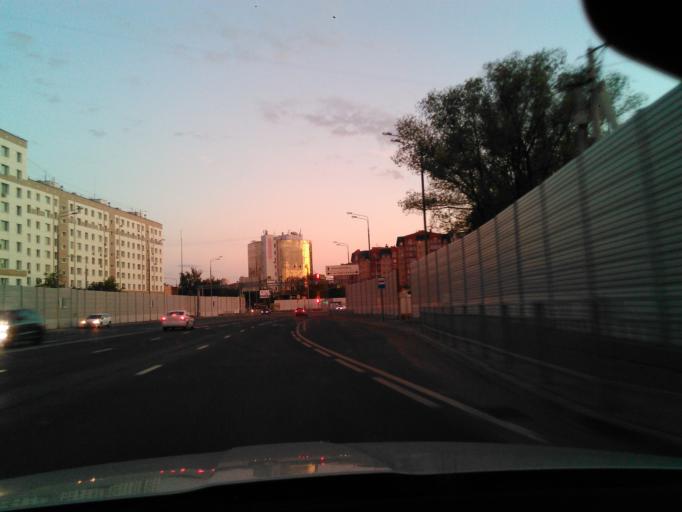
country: RU
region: Moskovskaya
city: Dolgoprudnyy
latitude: 55.9494
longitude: 37.5081
